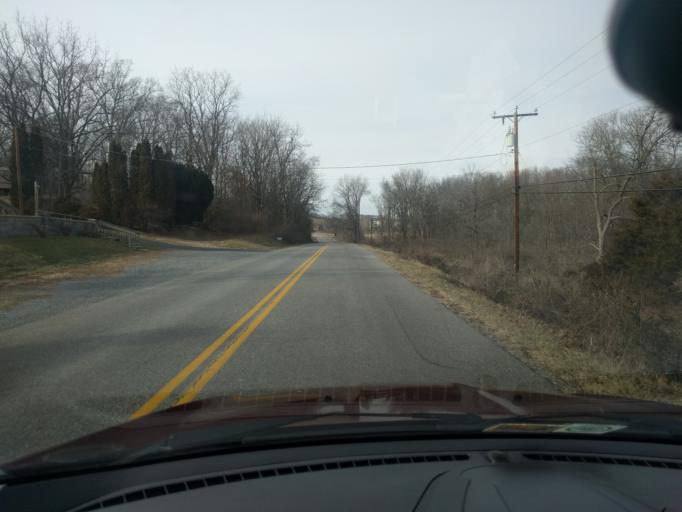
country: US
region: Virginia
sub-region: Augusta County
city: Stuarts Draft
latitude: 37.9274
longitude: -79.2071
